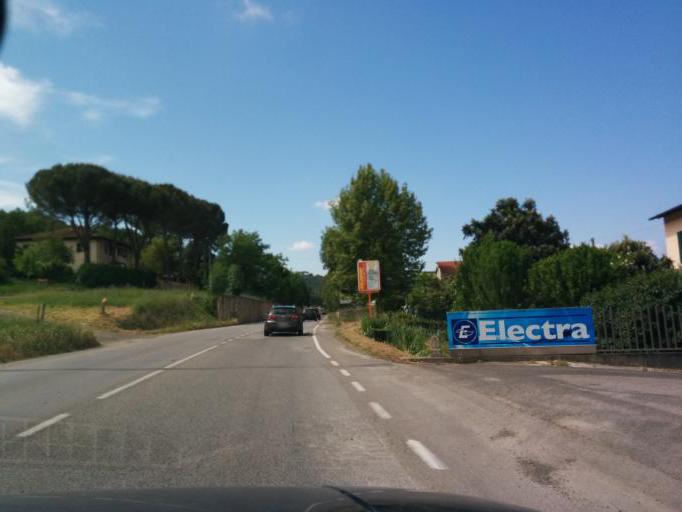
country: IT
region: Tuscany
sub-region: Provincia di Siena
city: Poggibonsi
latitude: 43.4672
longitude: 11.1262
